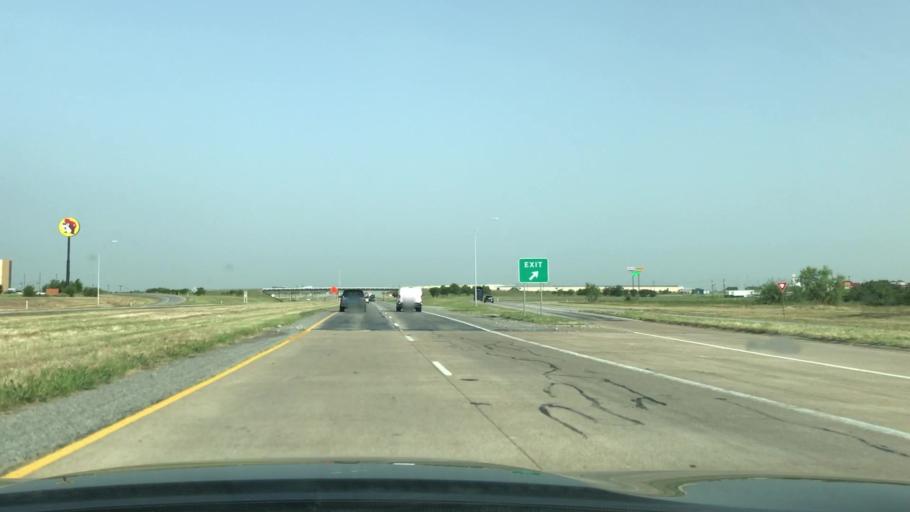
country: US
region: Texas
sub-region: Kaufman County
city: Terrell
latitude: 32.7189
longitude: -96.3148
